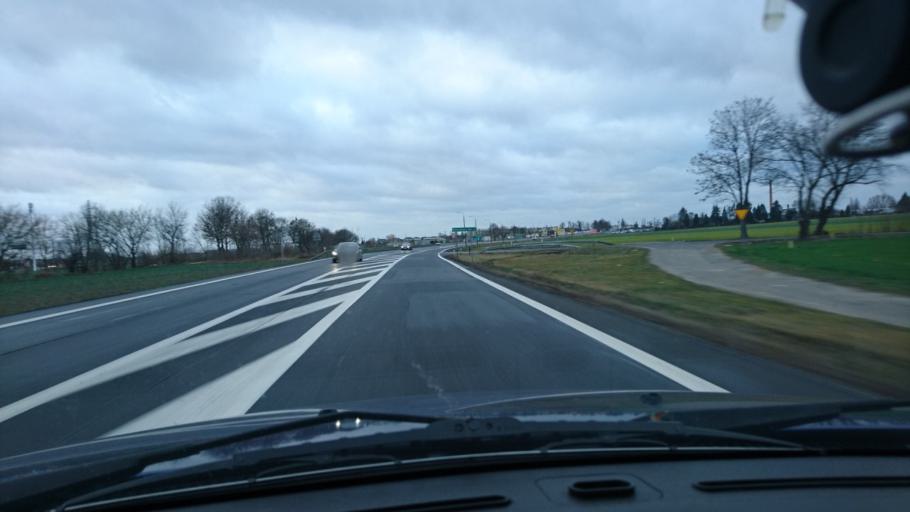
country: PL
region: Opole Voivodeship
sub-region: Powiat kluczborski
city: Kluczbork
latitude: 50.9912
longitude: 18.2167
